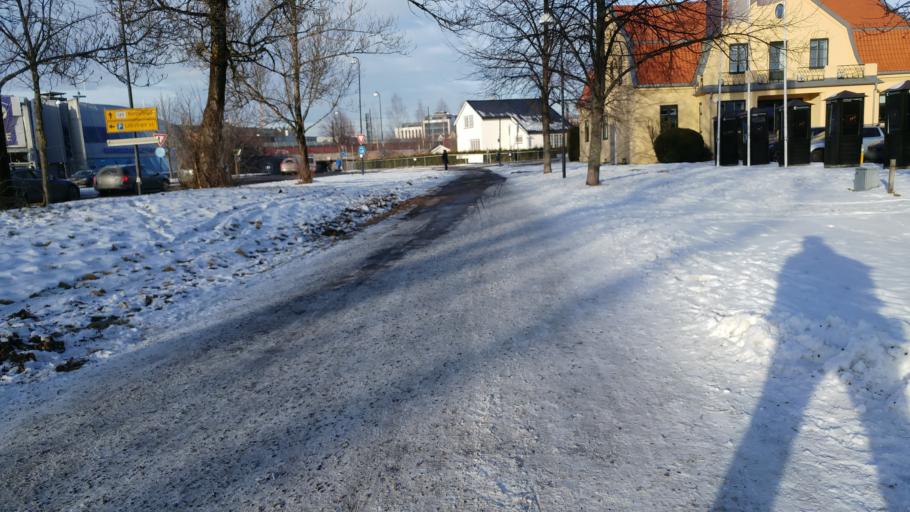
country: NO
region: Akershus
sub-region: Skedsmo
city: Lillestrom
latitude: 59.9523
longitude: 11.0512
